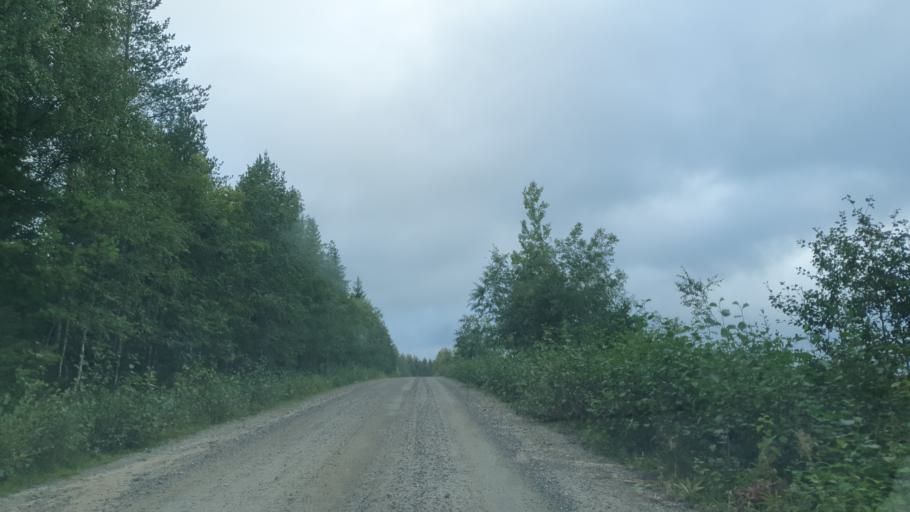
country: FI
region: Kainuu
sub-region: Kehys-Kainuu
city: Kuhmo
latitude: 64.1385
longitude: 29.5949
